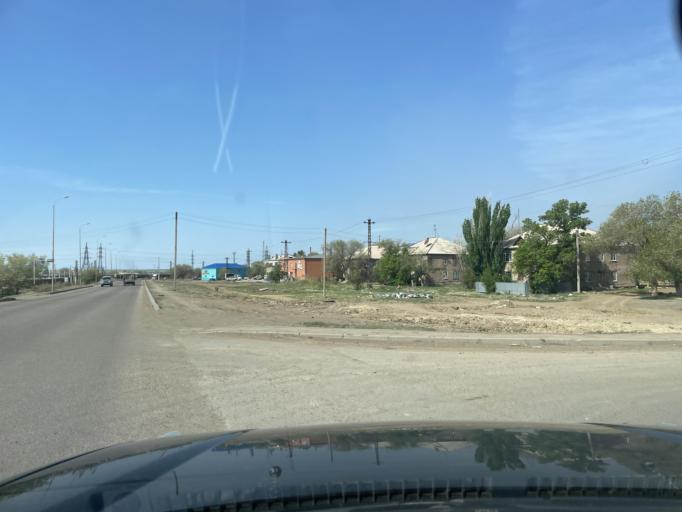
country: KZ
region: Qaraghandy
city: Zhezqazghan
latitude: 47.7835
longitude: 67.7036
